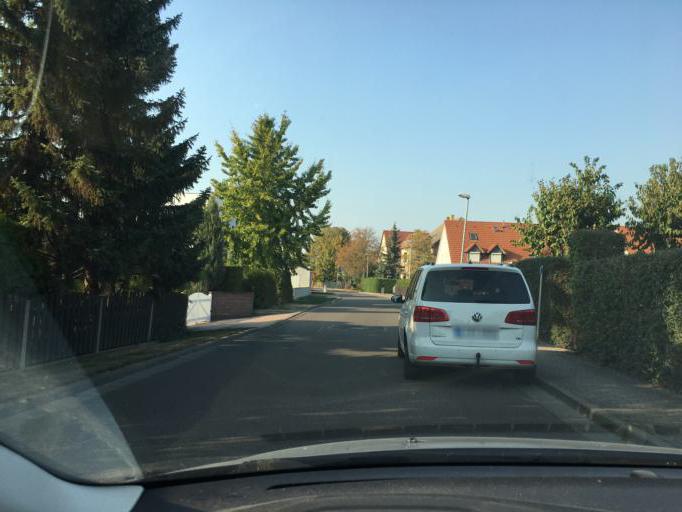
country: DE
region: Saxony
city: Wurzen
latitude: 51.3593
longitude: 12.7435
